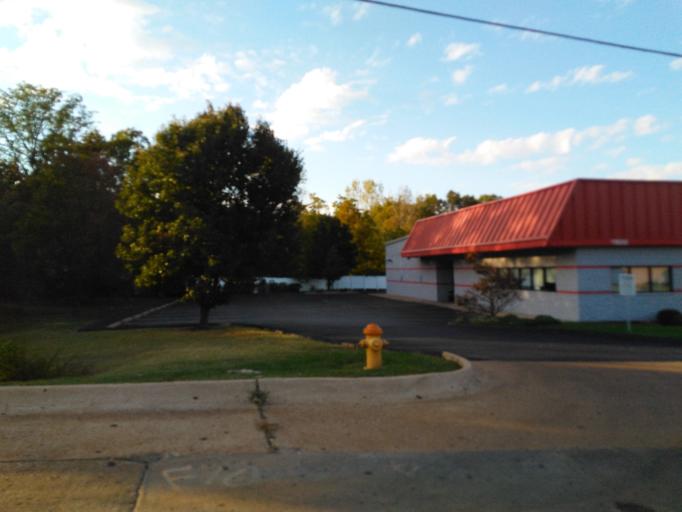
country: US
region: Missouri
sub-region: Saint Louis County
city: Sappington
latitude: 38.5345
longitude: -90.3827
